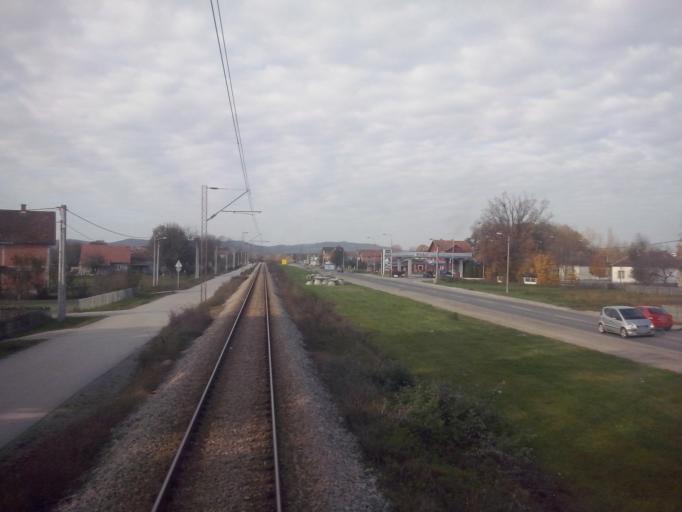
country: RS
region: Central Serbia
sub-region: Kolubarski Okrug
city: Lajkovac
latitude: 44.3648
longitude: 20.1487
